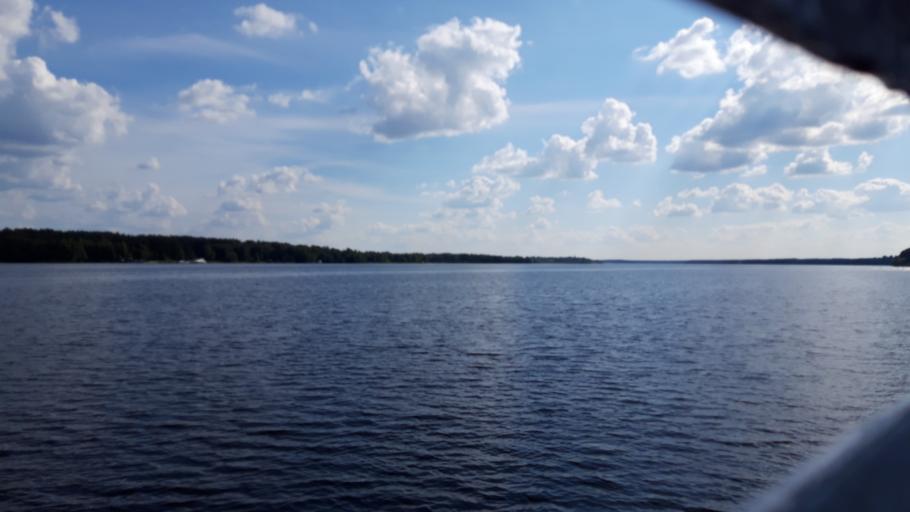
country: RU
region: Tverskaya
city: Konakovo
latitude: 56.6609
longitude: 36.6446
